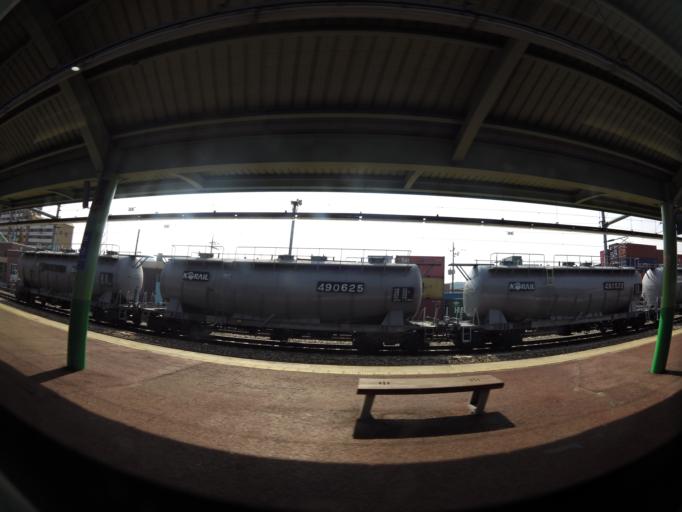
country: KR
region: Daejeon
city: Sintansin
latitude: 36.5325
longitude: 127.3651
